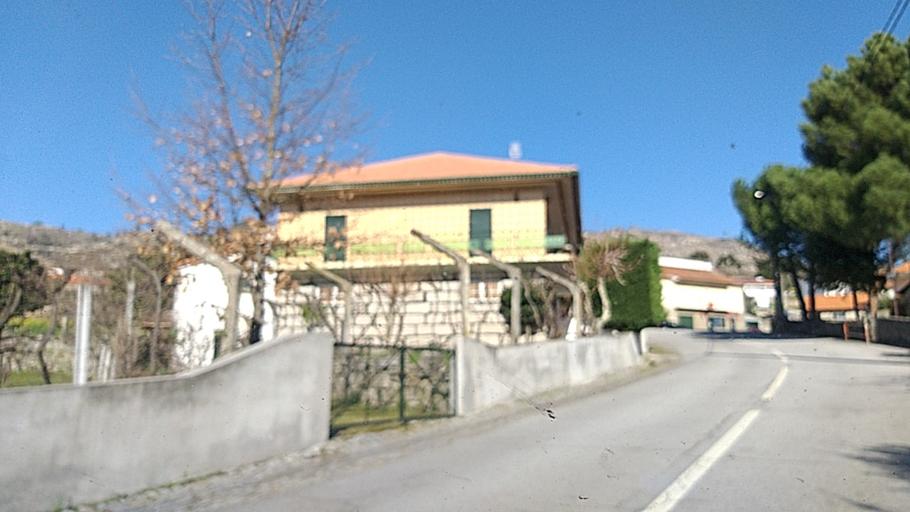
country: PT
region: Guarda
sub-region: Celorico da Beira
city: Celorico da Beira
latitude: 40.6572
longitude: -7.4649
